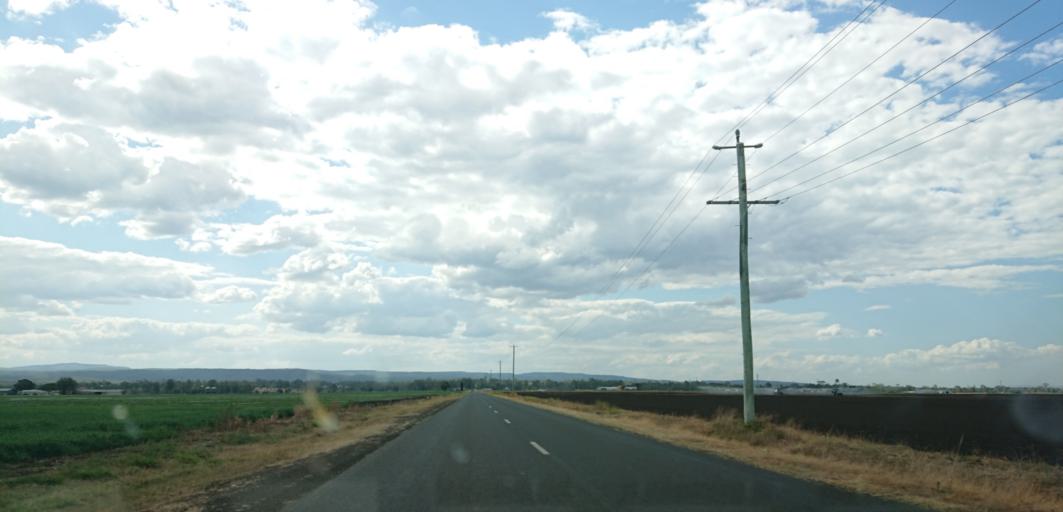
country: AU
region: Queensland
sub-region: Lockyer Valley
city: Gatton
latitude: -27.5891
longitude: 152.2274
